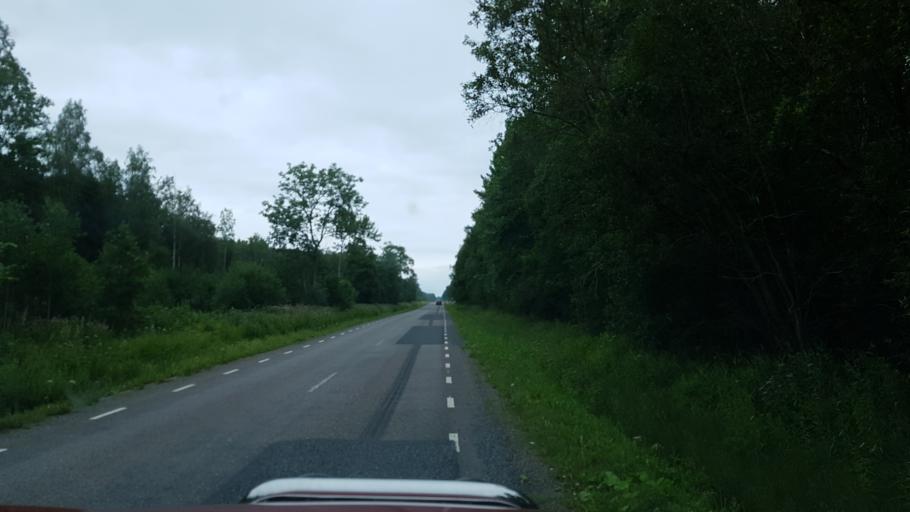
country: EE
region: Ida-Virumaa
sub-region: Johvi vald
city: Johvi
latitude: 59.4082
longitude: 27.4129
